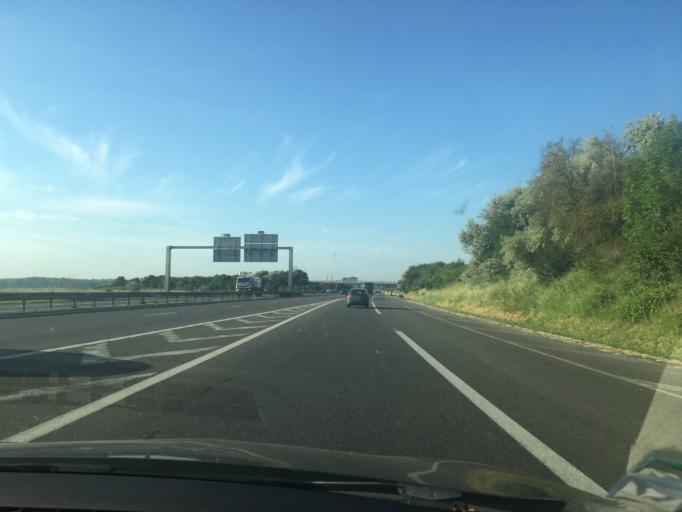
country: FR
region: Ile-de-France
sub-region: Departement de Seine-et-Marne
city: Vert-Saint-Denis
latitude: 48.5857
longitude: 2.6368
